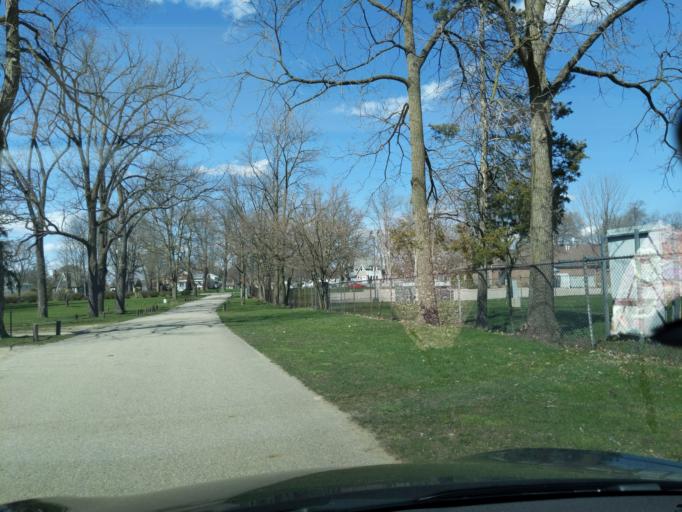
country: US
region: Michigan
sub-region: Ingham County
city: Mason
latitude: 42.5768
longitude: -84.4310
